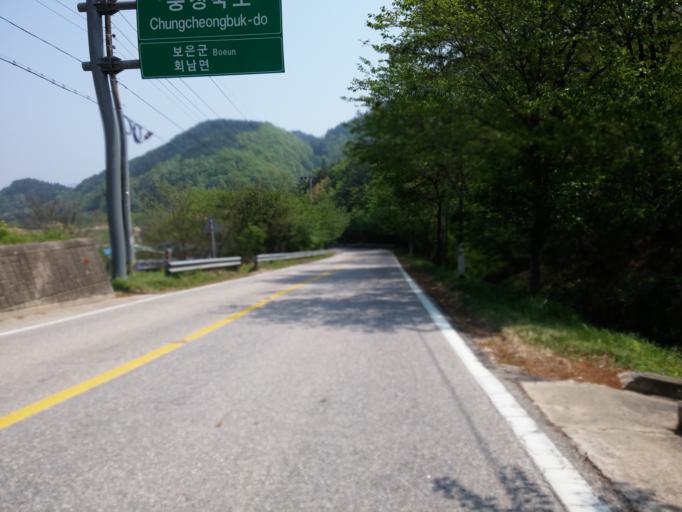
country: KR
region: Daejeon
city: Sintansin
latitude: 36.4206
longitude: 127.5290
